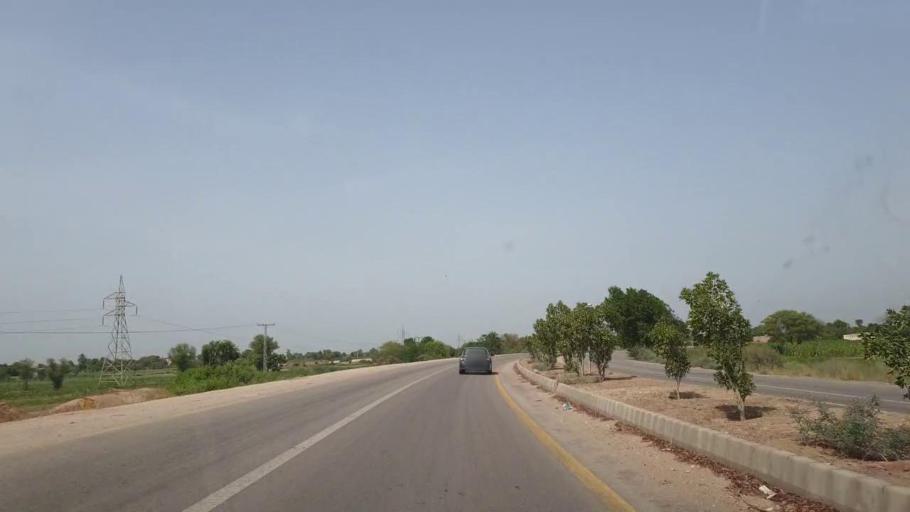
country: PK
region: Sindh
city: Sakrand
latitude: 26.1943
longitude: 68.2927
